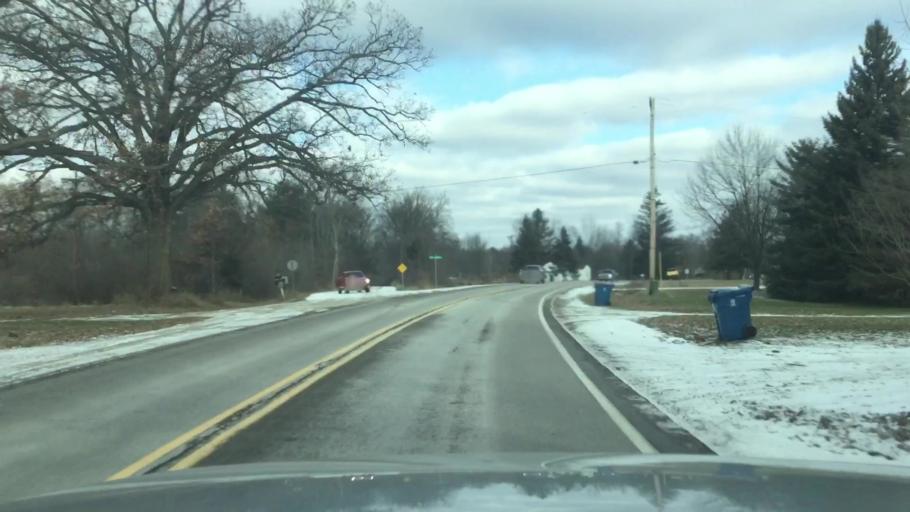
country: US
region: Michigan
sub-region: Genesee County
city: Linden
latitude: 42.8492
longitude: -83.7833
